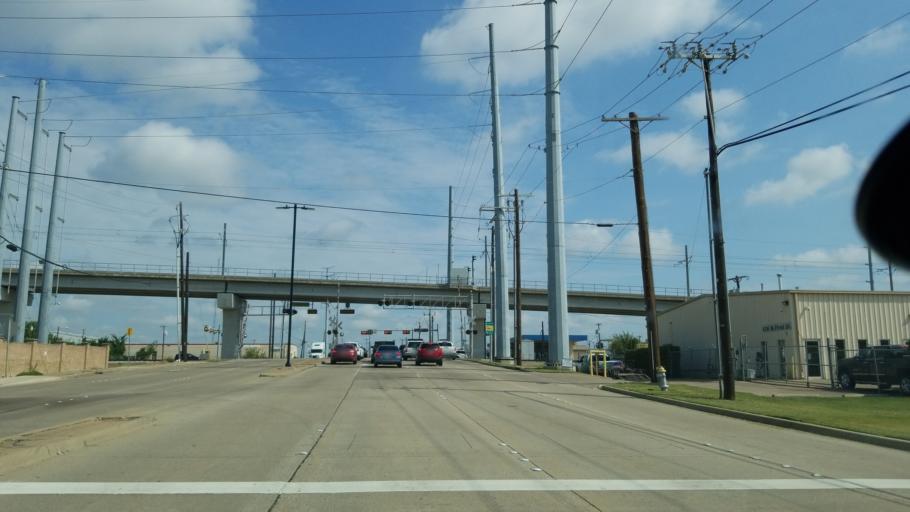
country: US
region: Texas
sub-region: Dallas County
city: Garland
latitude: 32.9160
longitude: -96.6307
